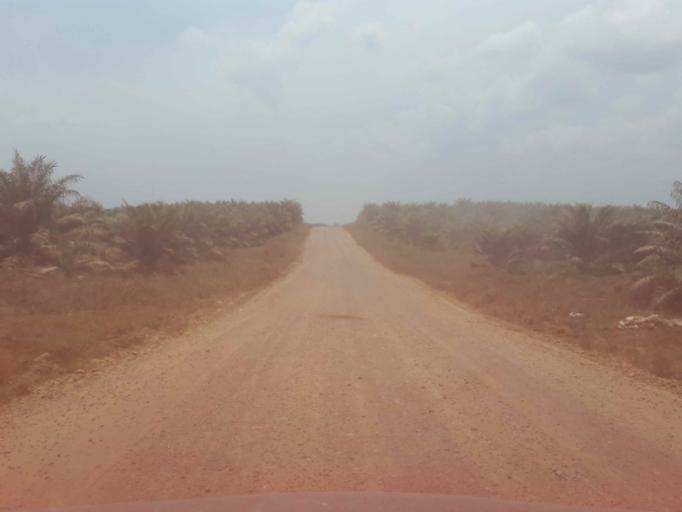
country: MY
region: Sarawak
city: Simanggang
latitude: 0.9985
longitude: 111.8862
